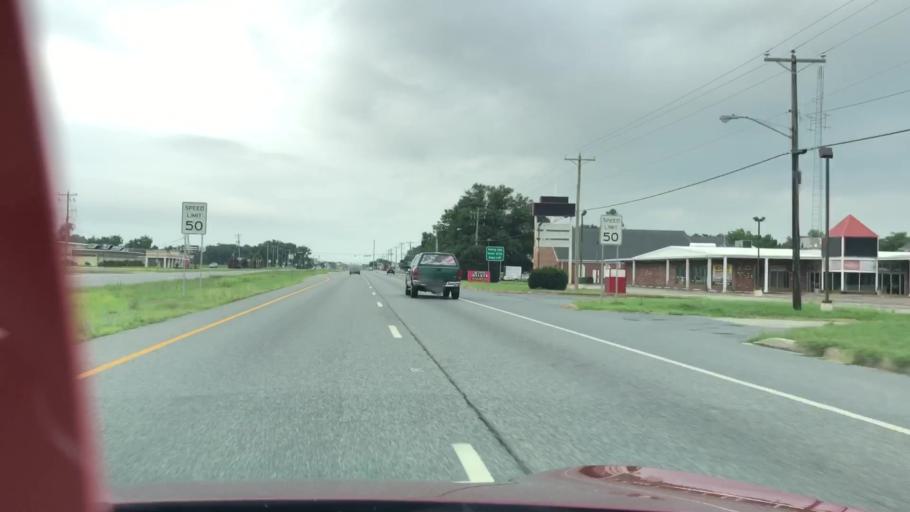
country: US
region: Delaware
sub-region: Kent County
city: Camden
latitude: 39.1182
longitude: -75.5352
